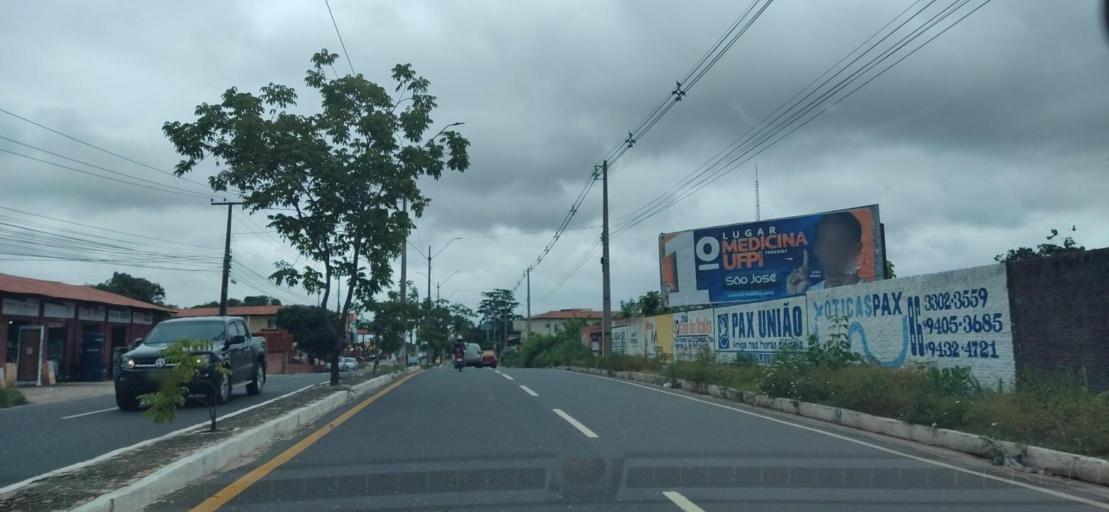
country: BR
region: Piaui
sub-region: Teresina
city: Teresina
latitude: -5.0556
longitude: -42.7470
